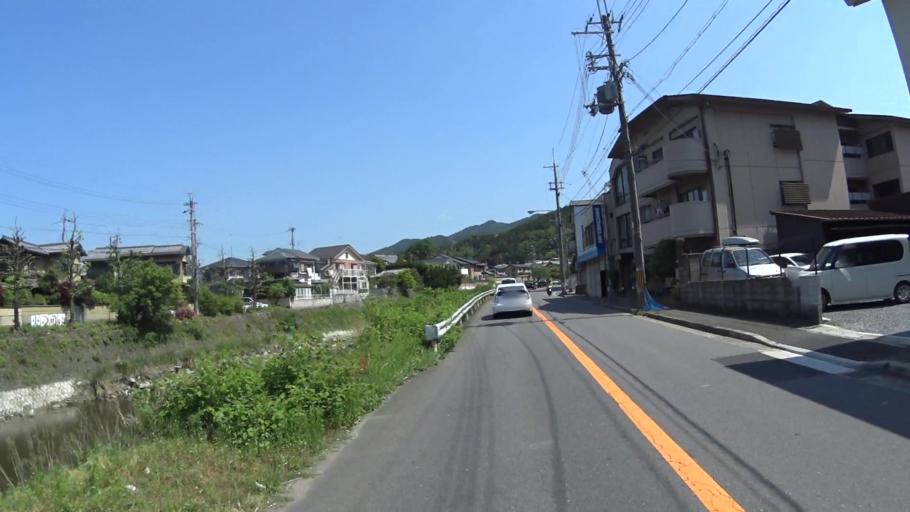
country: JP
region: Kyoto
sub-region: Kyoto-shi
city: Kamigyo-ku
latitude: 35.0615
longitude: 135.7935
